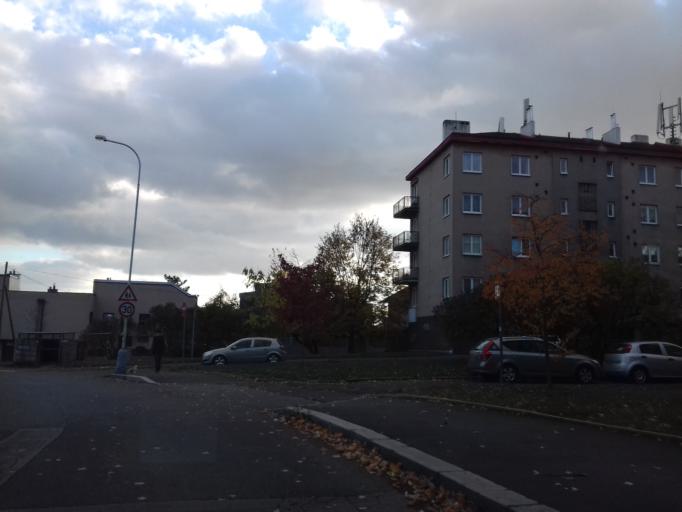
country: CZ
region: Praha
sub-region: Praha 4
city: Hodkovicky
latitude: 50.0240
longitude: 14.4131
